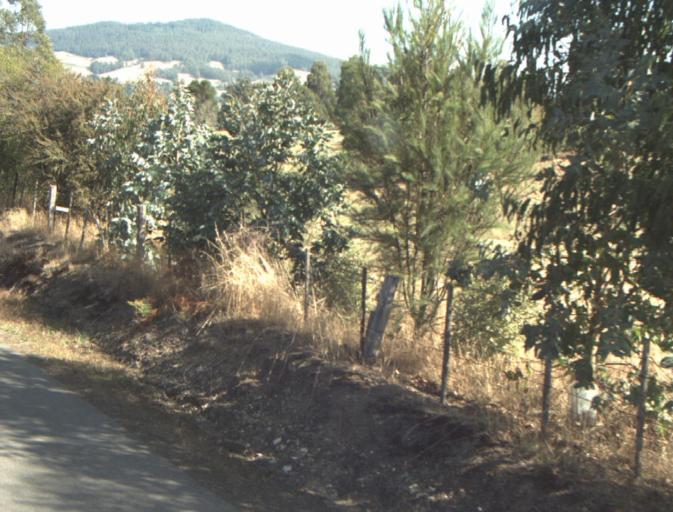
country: AU
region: Tasmania
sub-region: Launceston
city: Mayfield
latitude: -41.2356
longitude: 147.2344
